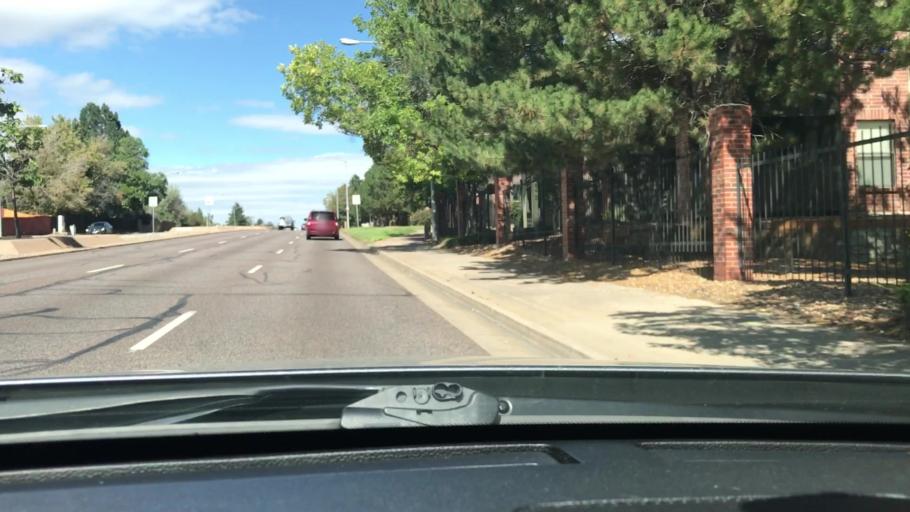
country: US
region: Colorado
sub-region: Arapahoe County
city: Dove Valley
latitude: 39.6353
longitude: -104.8102
